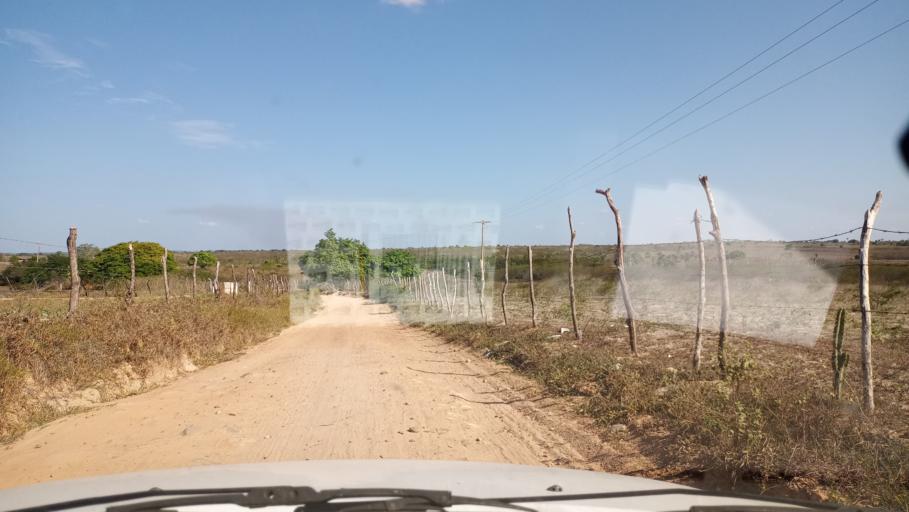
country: BR
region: Rio Grande do Norte
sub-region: Brejinho
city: Brejinho
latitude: -6.1792
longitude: -35.4531
